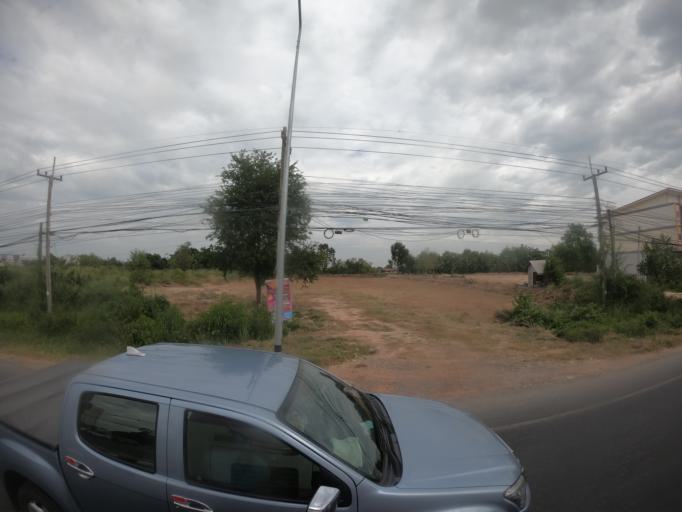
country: TH
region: Maha Sarakham
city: Maha Sarakham
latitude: 16.2079
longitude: 103.2853
